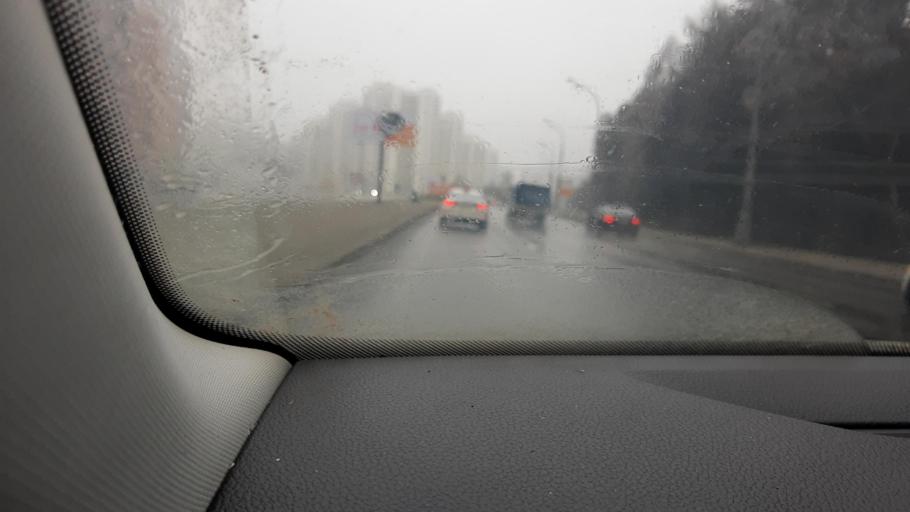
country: RU
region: Moscow
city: Chertanovo Yuzhnoye
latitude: 55.5588
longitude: 37.5540
